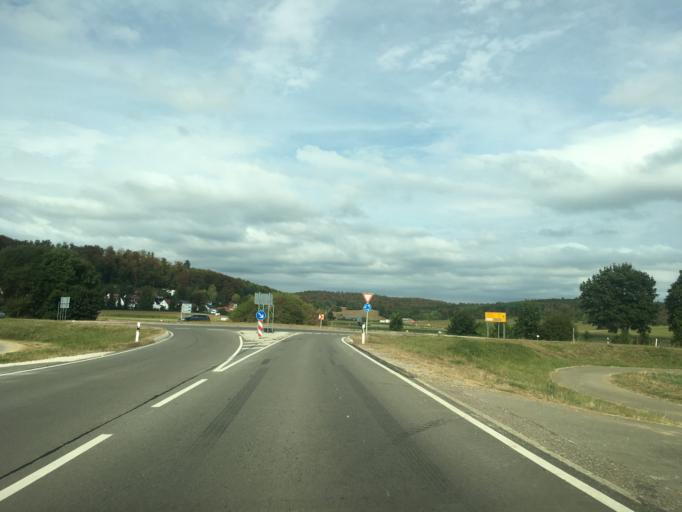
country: DE
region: Baden-Wuerttemberg
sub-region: Tuebingen Region
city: Pfullingen
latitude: 48.3998
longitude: 9.2756
